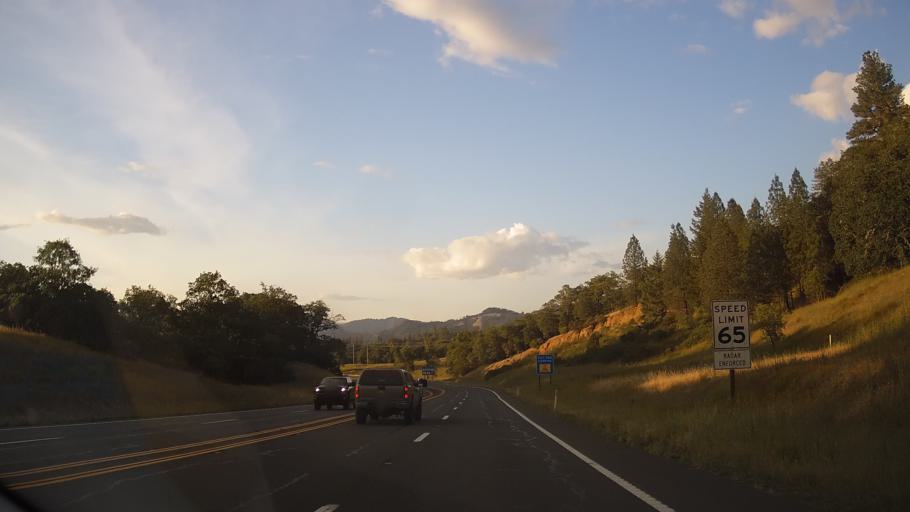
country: US
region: California
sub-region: Mendocino County
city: Willits
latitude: 39.3598
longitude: -123.3162
